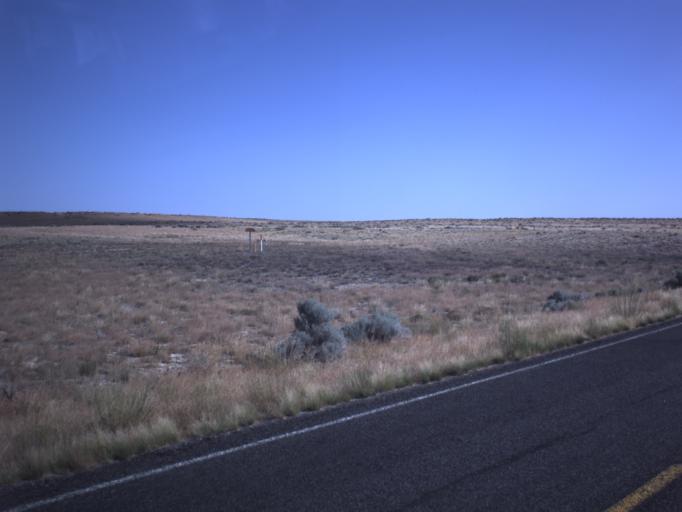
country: US
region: Utah
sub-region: Millard County
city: Fillmore
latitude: 38.8985
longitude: -112.8232
